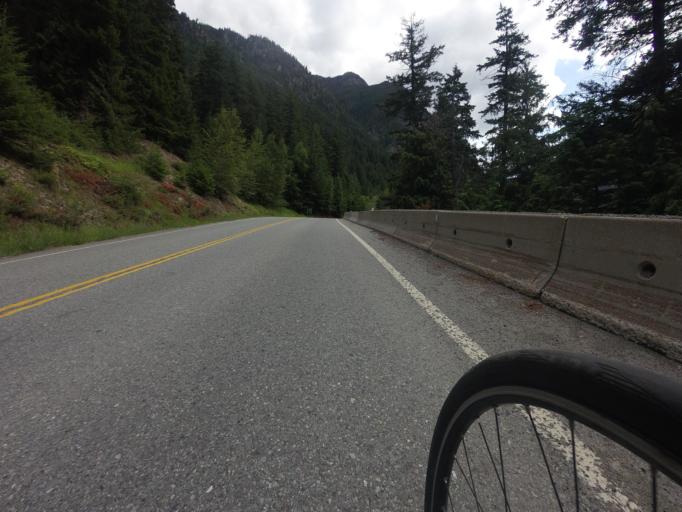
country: CA
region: British Columbia
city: Lillooet
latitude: 50.6329
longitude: -122.0892
